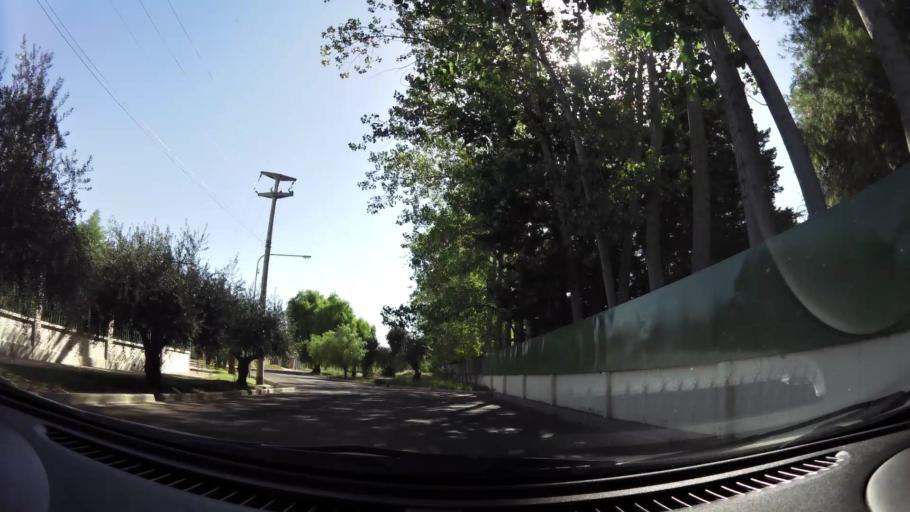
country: AR
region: Mendoza
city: Villa Nueva
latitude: -32.9105
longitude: -68.7893
